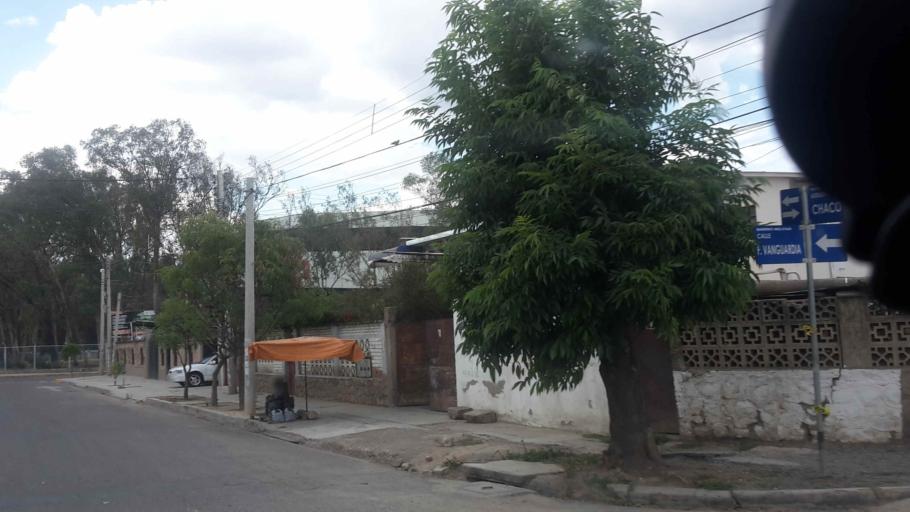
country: BO
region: Cochabamba
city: Cochabamba
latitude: -17.4029
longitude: -66.1740
